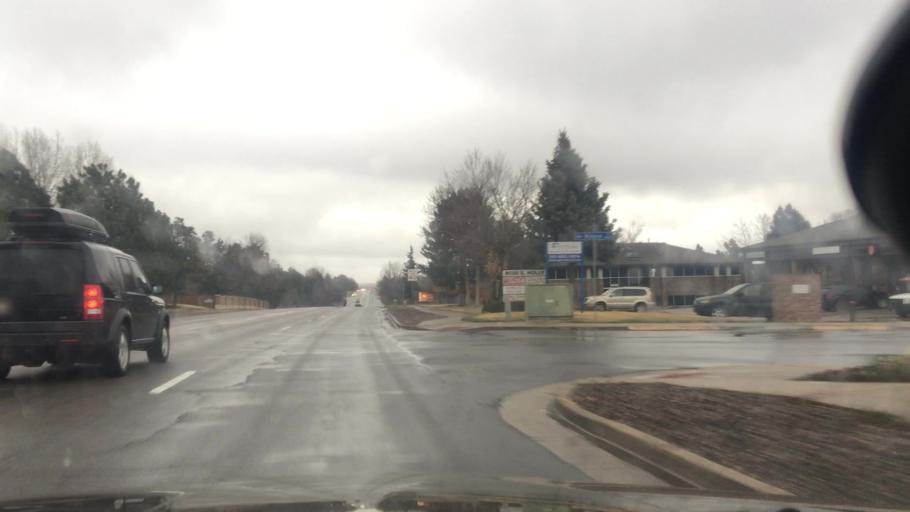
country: US
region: Colorado
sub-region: Arapahoe County
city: Castlewood
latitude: 39.5723
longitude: -104.9230
